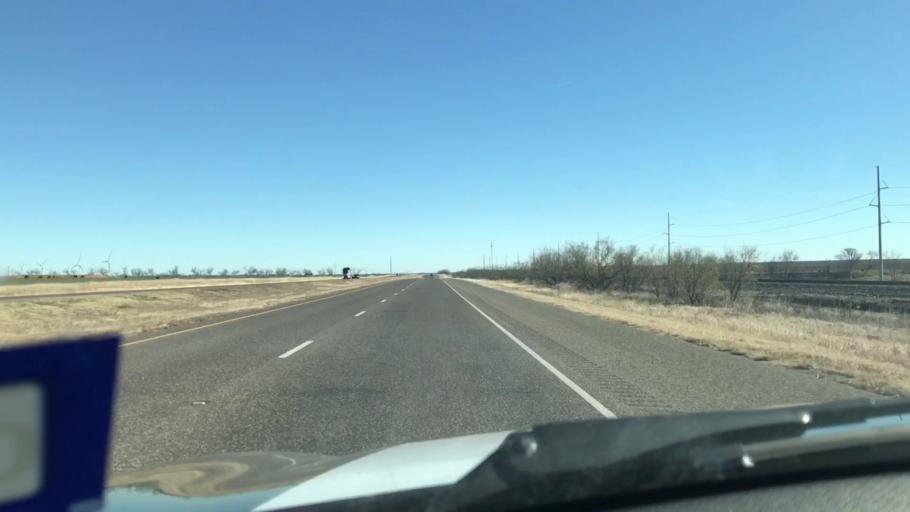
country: US
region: Texas
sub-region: Scurry County
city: Snyder
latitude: 32.8726
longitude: -101.0415
